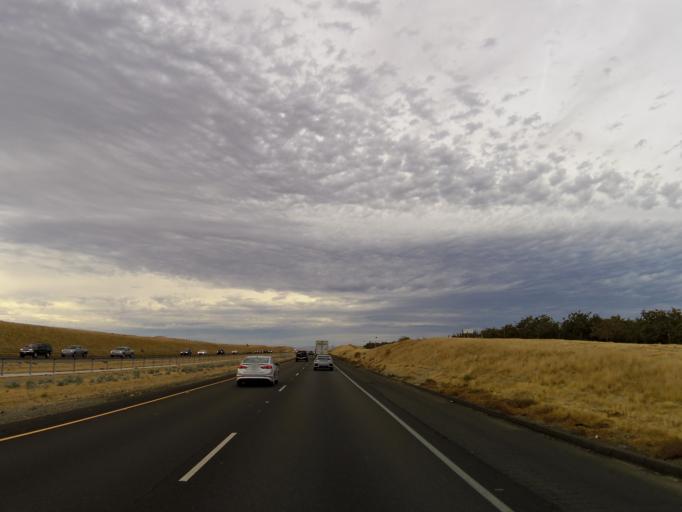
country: US
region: California
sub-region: Kings County
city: Kettleman City
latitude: 36.0379
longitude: -120.0357
